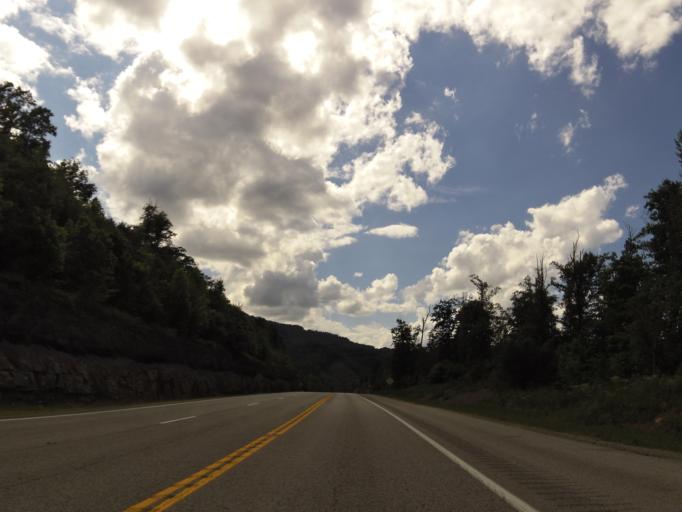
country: US
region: Kentucky
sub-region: Harlan County
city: Harlan
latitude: 36.7901
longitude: -83.2529
